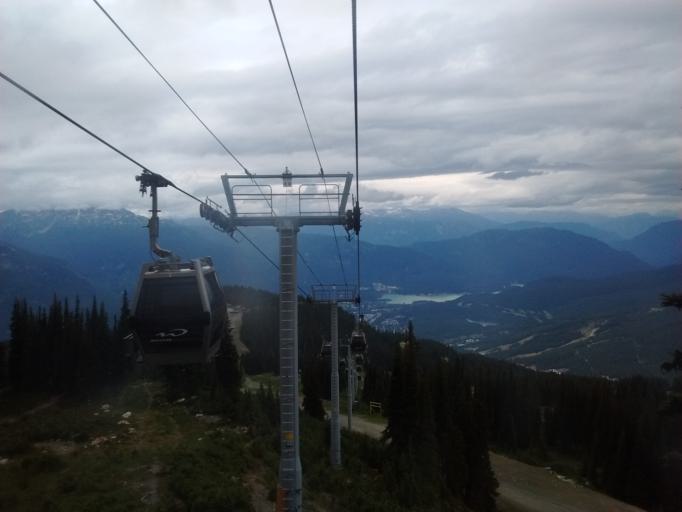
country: CA
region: British Columbia
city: Whistler
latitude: 50.0709
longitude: -122.9472
